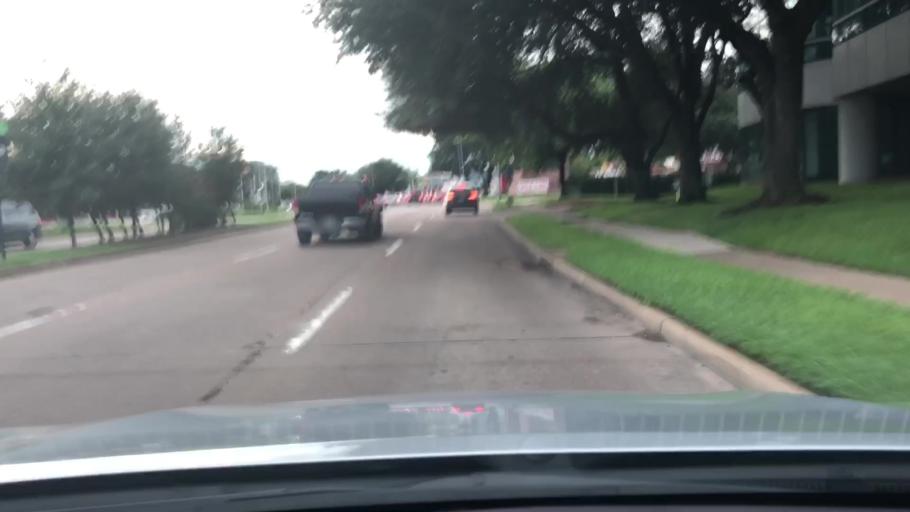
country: US
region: Texas
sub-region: Harris County
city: Piney Point Village
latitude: 29.7213
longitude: -95.5374
